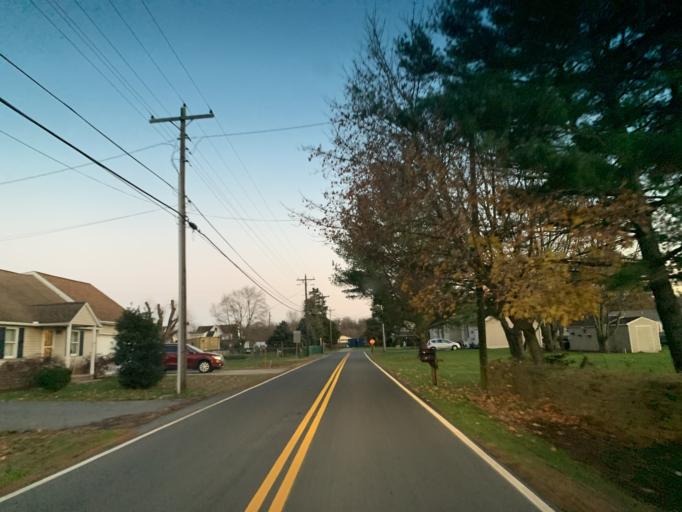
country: US
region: Delaware
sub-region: New Castle County
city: Middletown
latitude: 39.4176
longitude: -75.7792
